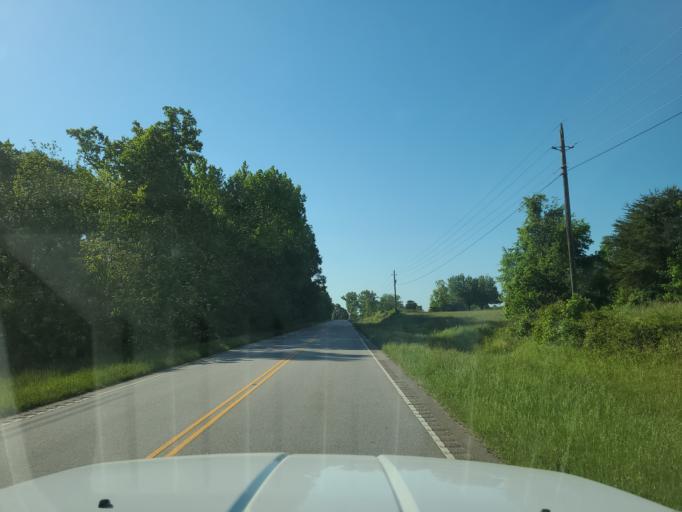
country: US
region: South Carolina
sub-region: York County
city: Clover
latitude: 35.1021
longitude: -81.2956
